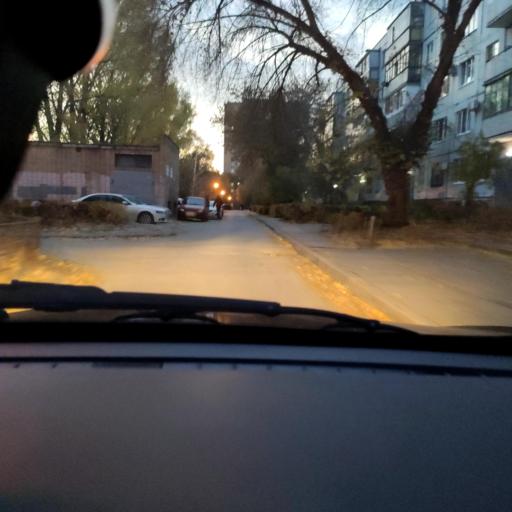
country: RU
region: Samara
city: Tol'yatti
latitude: 53.5320
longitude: 49.3026
